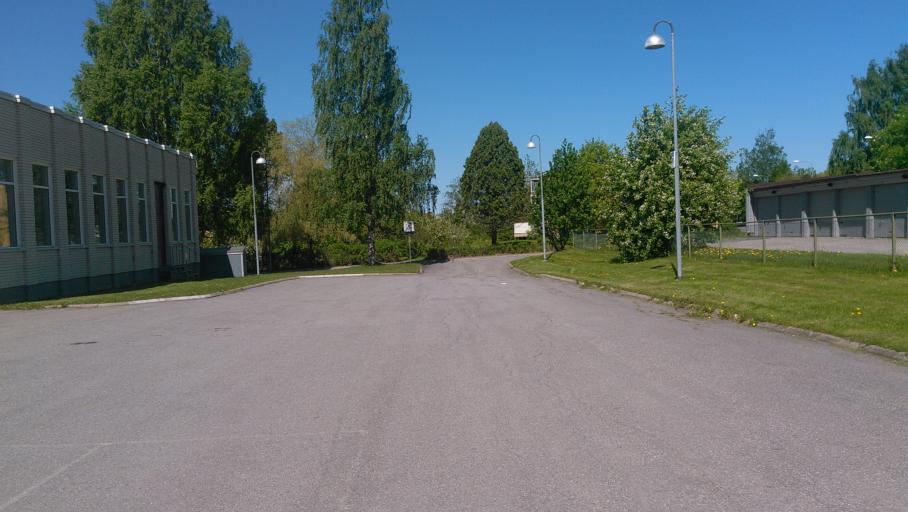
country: SE
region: Vaesterbotten
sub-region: Umea Kommun
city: Ersmark
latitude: 63.8409
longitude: 20.3210
